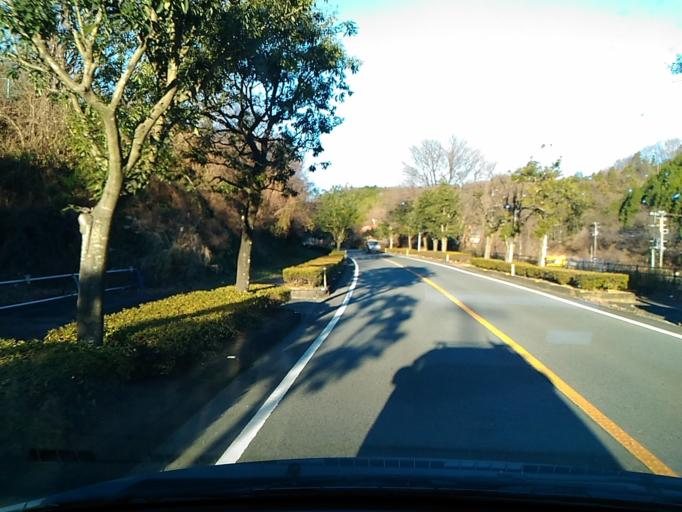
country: JP
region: Ibaraki
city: Kitaibaraki
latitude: 36.9097
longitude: 140.7456
